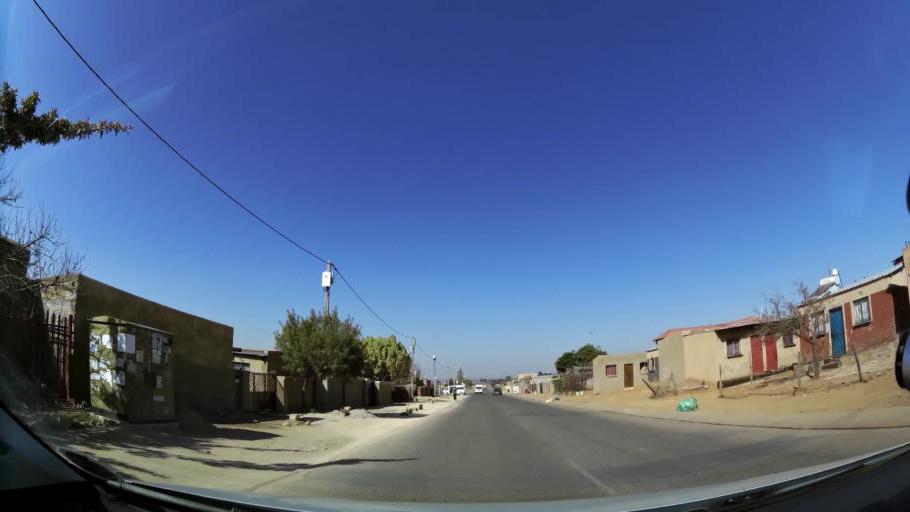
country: ZA
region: Gauteng
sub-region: Ekurhuleni Metropolitan Municipality
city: Tembisa
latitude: -26.0239
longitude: 28.2400
